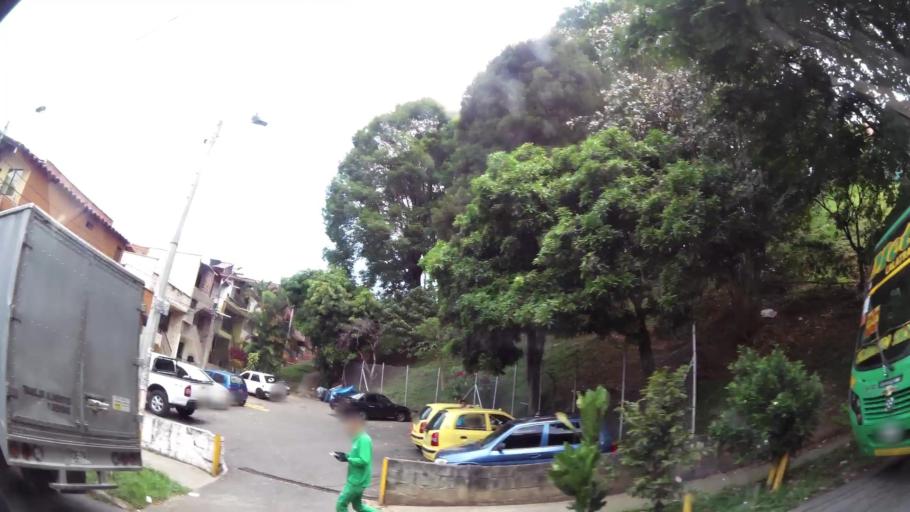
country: CO
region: Antioquia
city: Itagui
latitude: 6.1812
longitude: -75.6114
